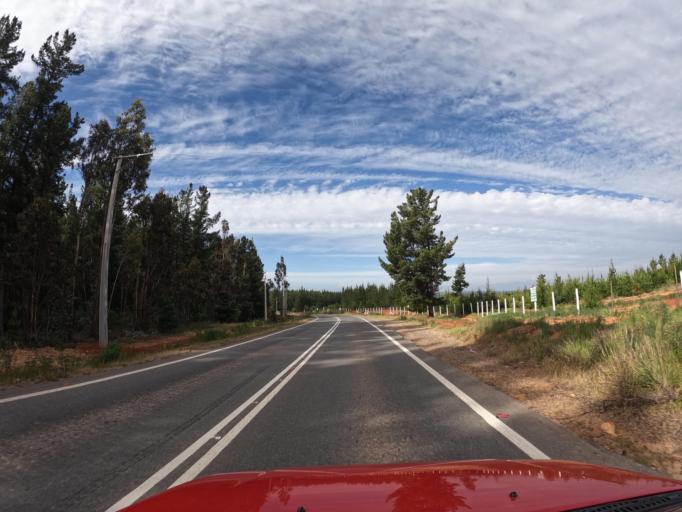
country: CL
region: O'Higgins
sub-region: Provincia de Colchagua
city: Santa Cruz
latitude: -34.3003
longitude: -71.8244
